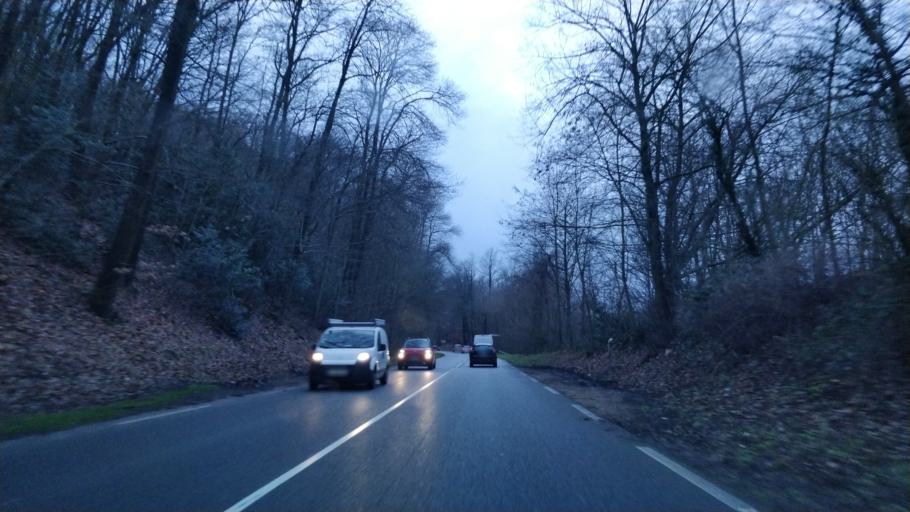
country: FR
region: Ile-de-France
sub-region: Departement de l'Essonne
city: Bures-sur-Yvette
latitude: 48.6927
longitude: 2.1740
